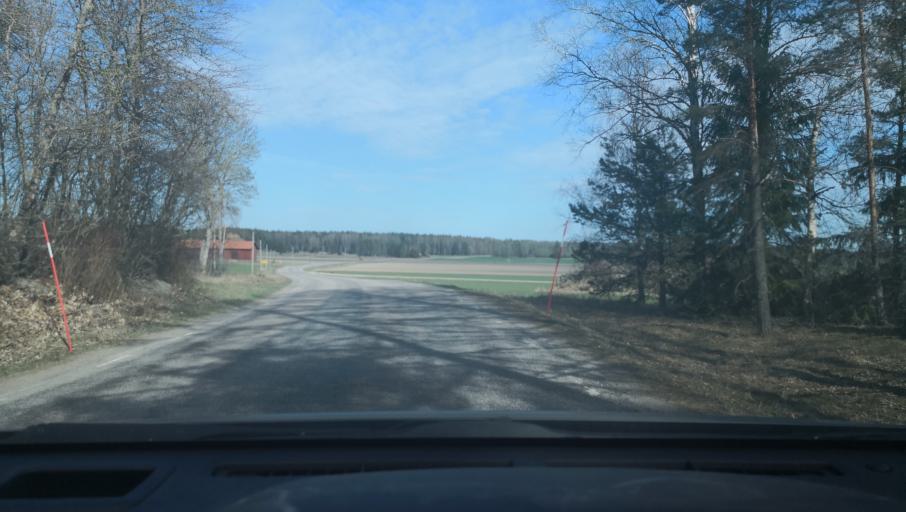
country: SE
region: Uppsala
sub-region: Enkopings Kommun
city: Irsta
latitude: 59.7800
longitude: 16.9485
